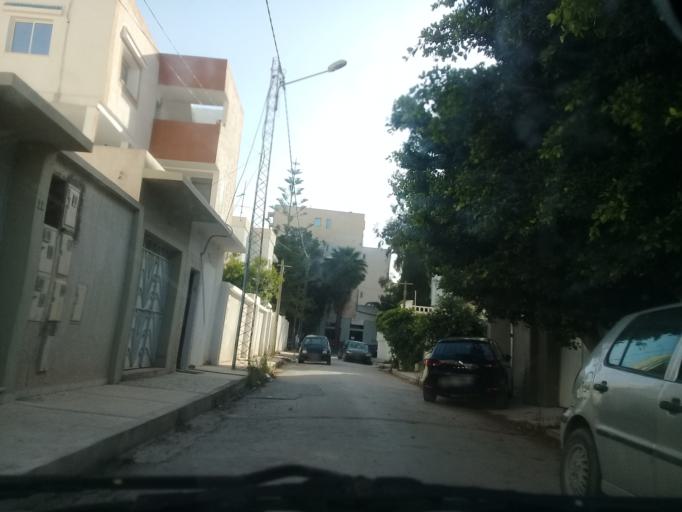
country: TN
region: Ariana
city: Ariana
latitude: 36.8361
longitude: 10.1944
